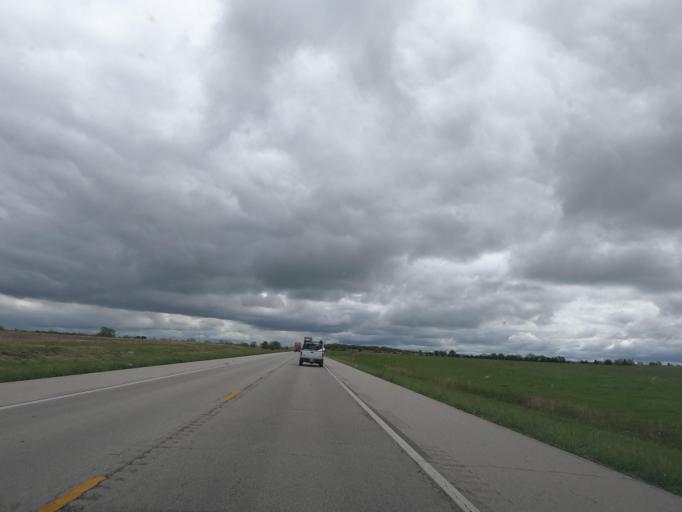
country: US
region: Kansas
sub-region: Wilson County
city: Fredonia
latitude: 37.5052
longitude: -95.7846
